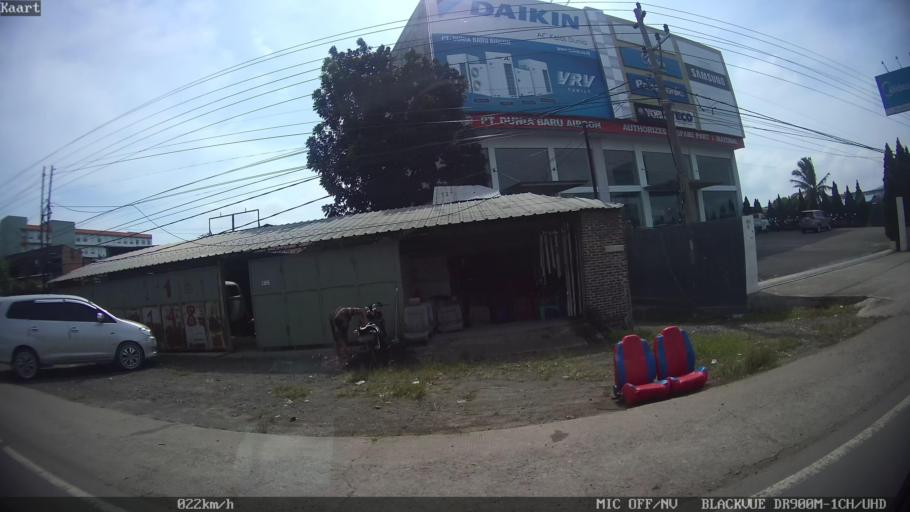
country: ID
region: Lampung
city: Kedaton
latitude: -5.3875
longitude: 105.2876
